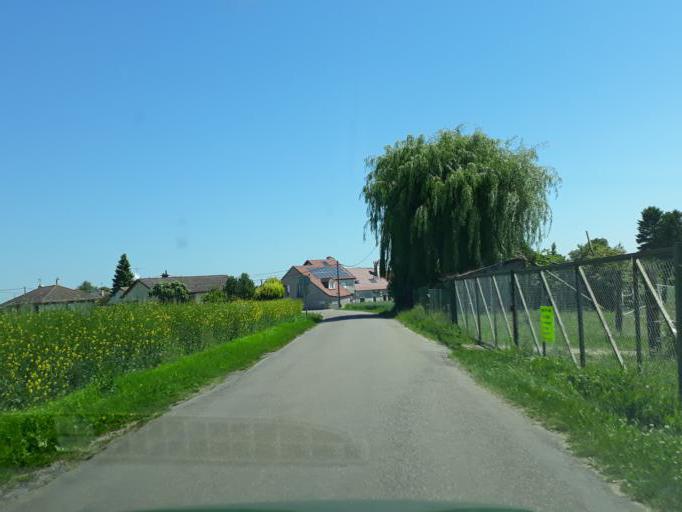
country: FR
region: Bourgogne
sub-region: Departement de la Cote-d'Or
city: Nuits-Saint-Georges
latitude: 47.1642
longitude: 4.9759
